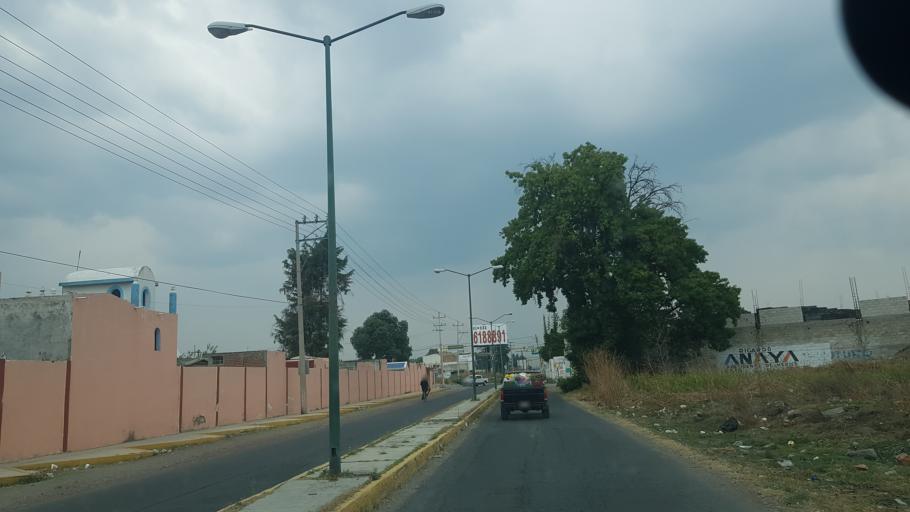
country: MX
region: Puebla
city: Huejotzingo
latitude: 19.1688
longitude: -98.4115
